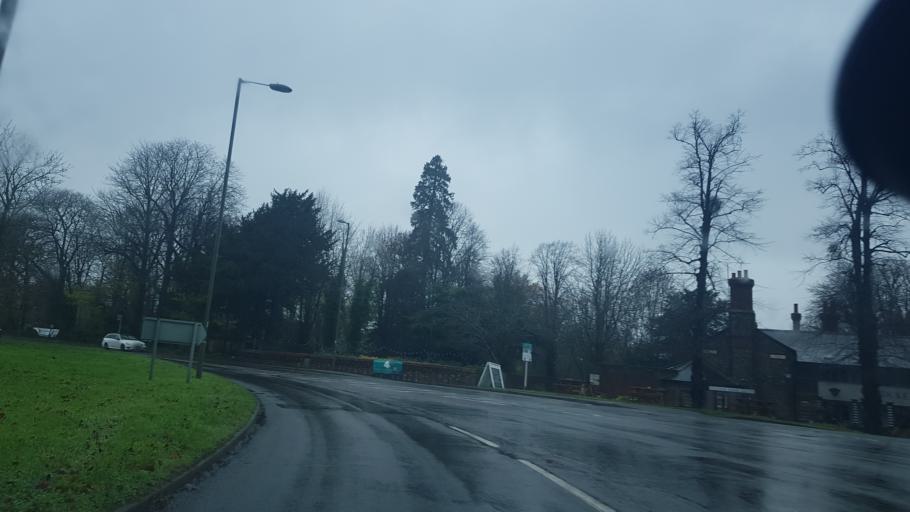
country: GB
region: England
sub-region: Surrey
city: East Horsley
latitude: 51.2624
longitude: -0.4314
